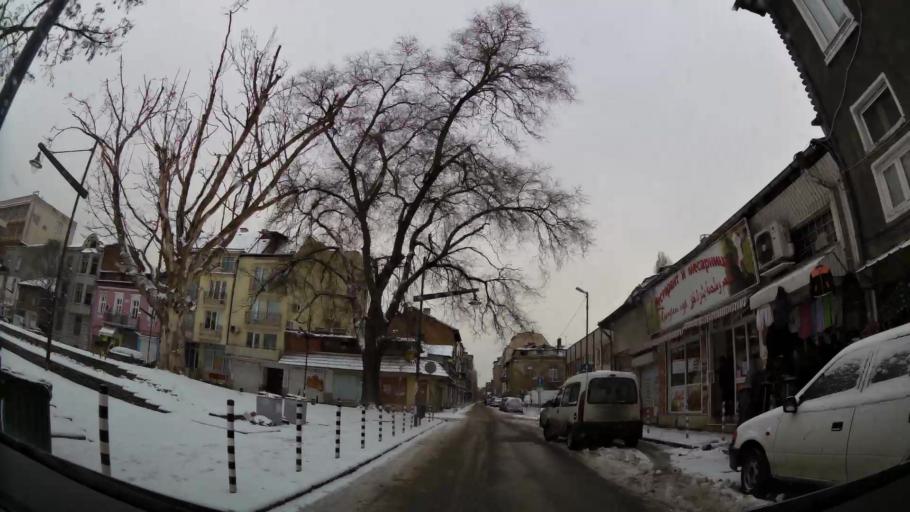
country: BG
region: Sofia-Capital
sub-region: Stolichna Obshtina
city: Sofia
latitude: 42.7034
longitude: 23.3200
